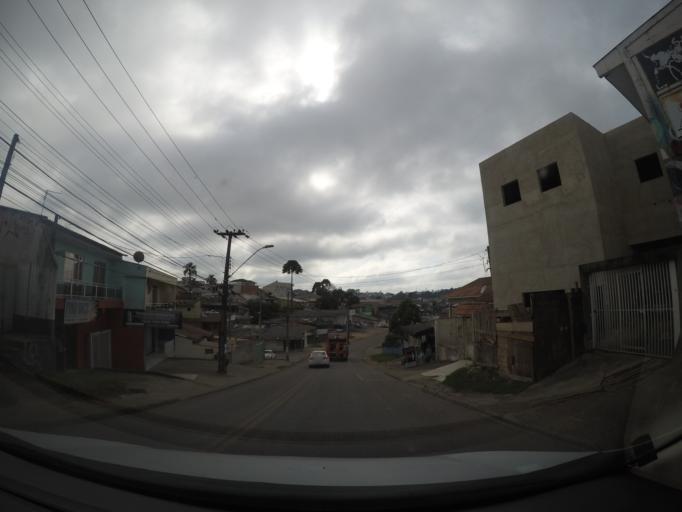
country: BR
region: Parana
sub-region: Colombo
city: Colombo
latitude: -25.3519
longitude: -49.2172
